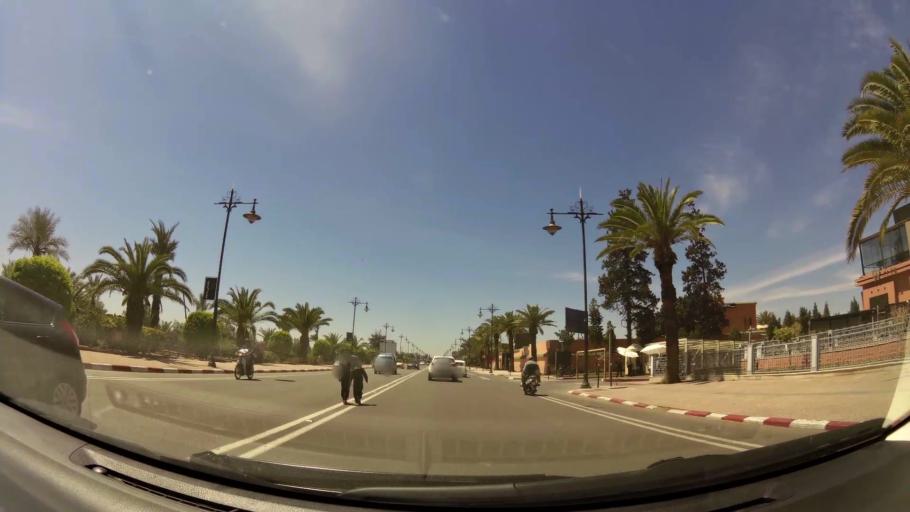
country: MA
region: Marrakech-Tensift-Al Haouz
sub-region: Marrakech
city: Marrakesh
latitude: 31.6175
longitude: -8.0095
